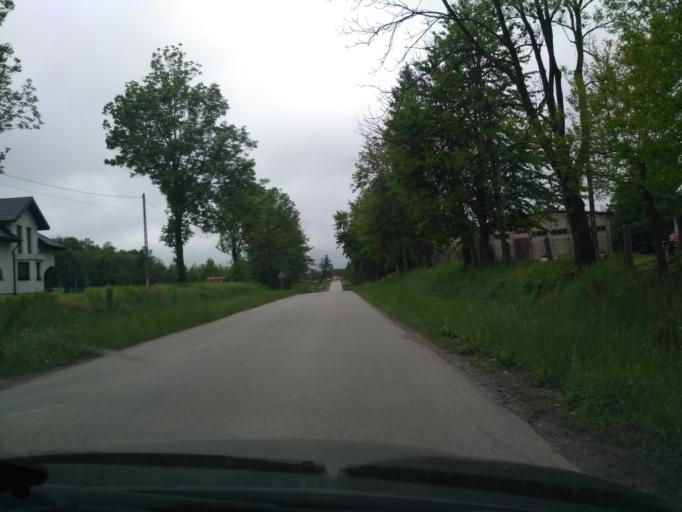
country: PL
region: Subcarpathian Voivodeship
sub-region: Powiat jasielski
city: Brzyska
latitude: 49.8365
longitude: 21.3921
